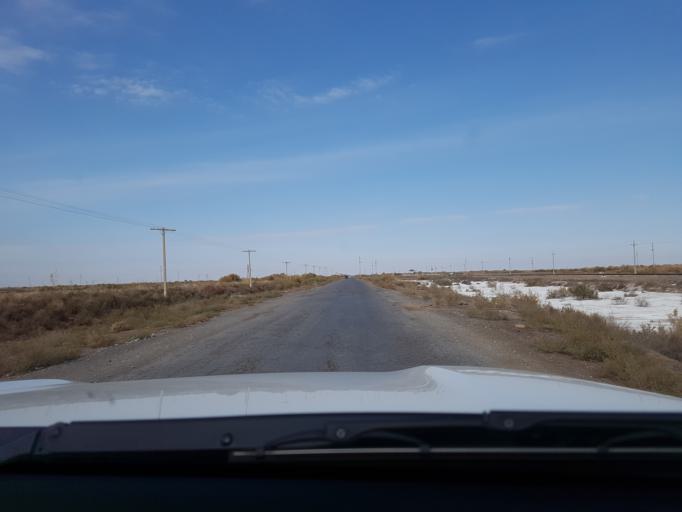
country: TM
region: Ahal
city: Tejen
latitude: 37.4430
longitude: 61.0929
